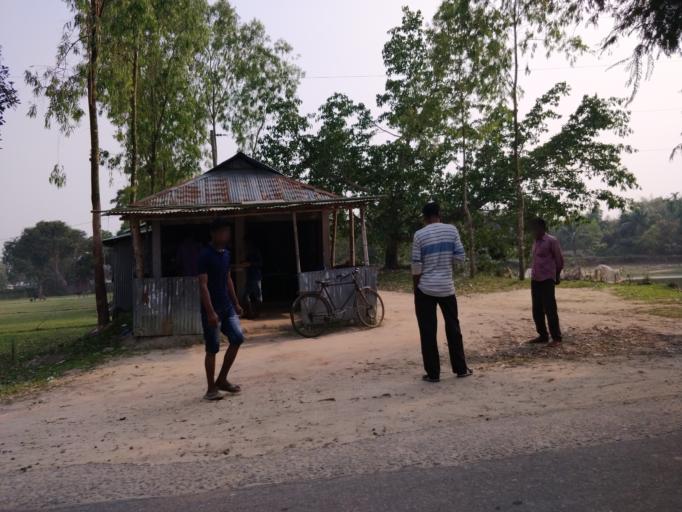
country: IN
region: Tripura
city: Khowai
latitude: 24.1293
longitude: 91.3706
